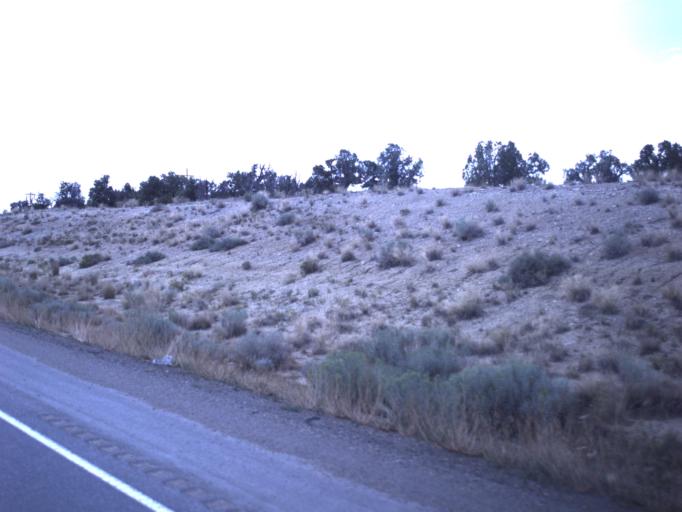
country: US
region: Utah
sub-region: Duchesne County
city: Duchesne
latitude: 40.1643
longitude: -110.4631
